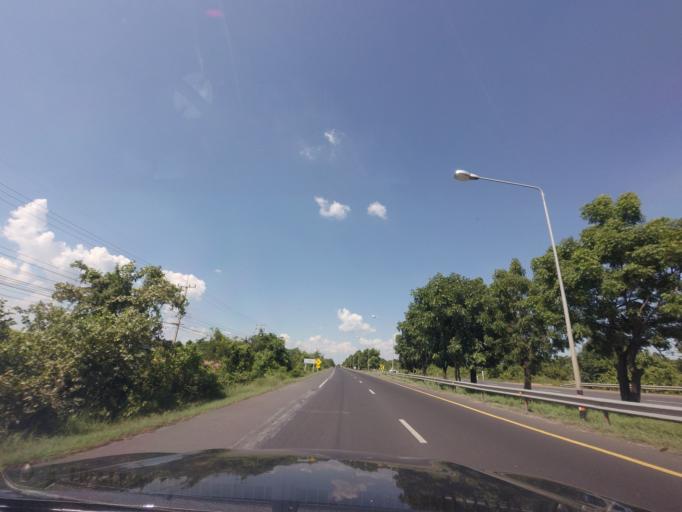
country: TH
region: Nakhon Ratchasima
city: Non Sung
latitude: 15.1930
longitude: 102.3483
